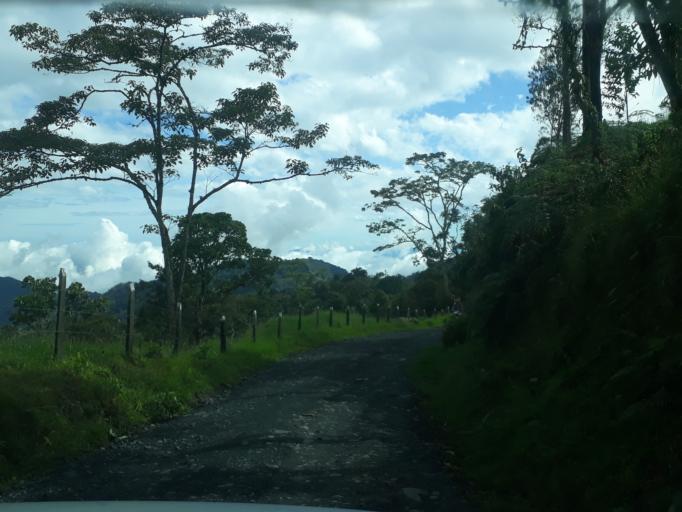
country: CO
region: Cundinamarca
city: La Mesa
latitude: 5.3346
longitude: -74.0568
